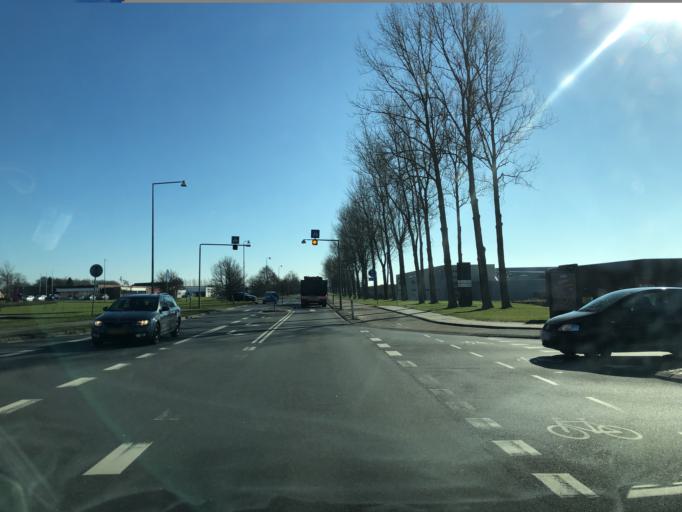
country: DK
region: Central Jutland
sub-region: Ikast-Brande Kommune
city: Ikast
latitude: 56.1319
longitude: 9.1660
